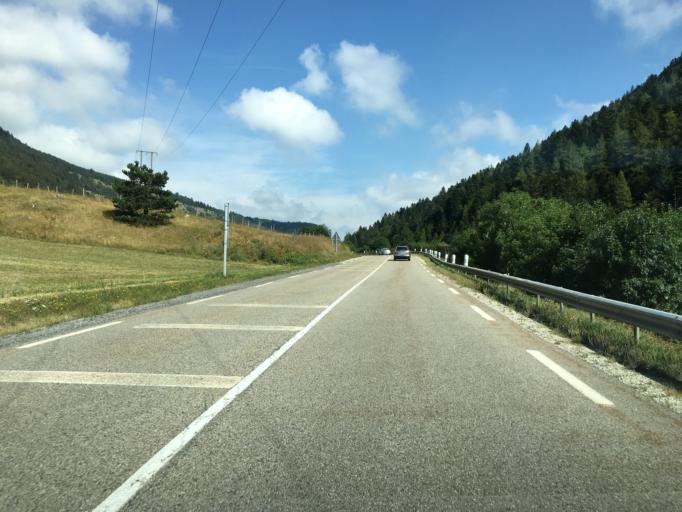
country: FR
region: Rhone-Alpes
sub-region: Departement de l'Isere
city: Mens
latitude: 44.7126
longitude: 5.6771
